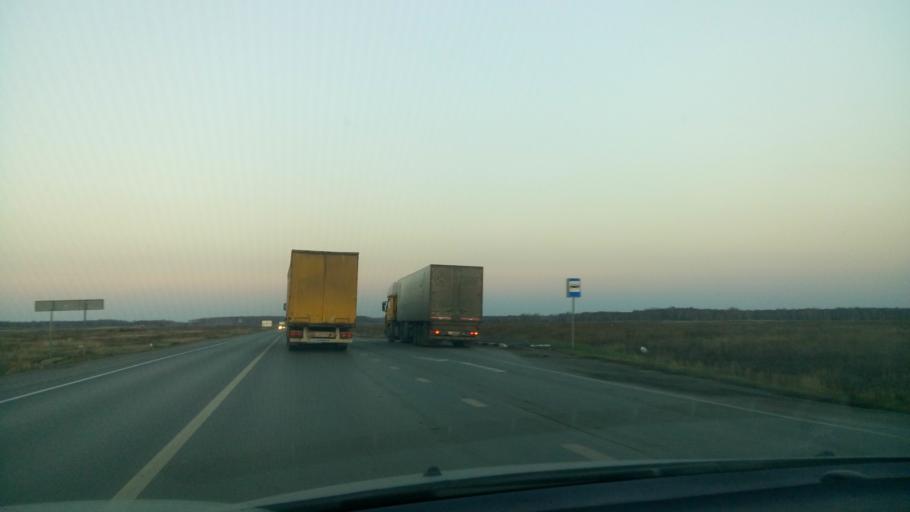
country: RU
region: Sverdlovsk
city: Pyshma
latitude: 56.9161
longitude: 63.1277
